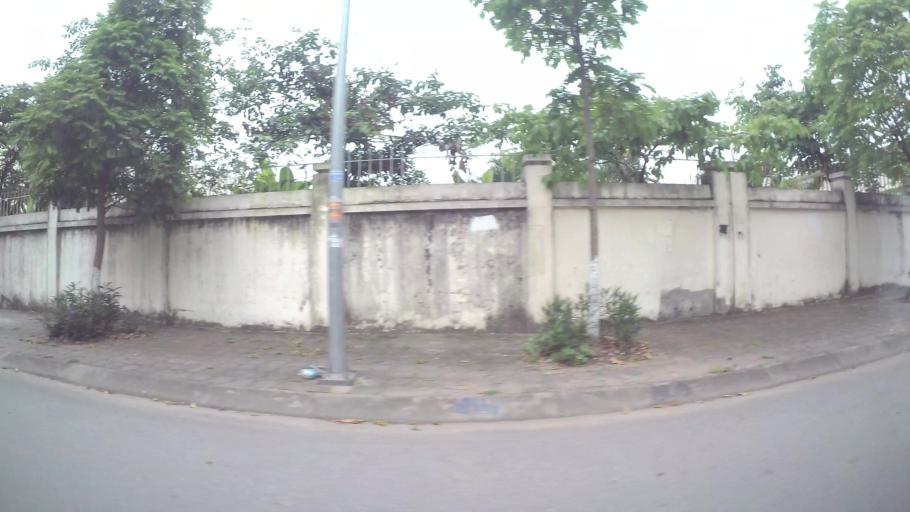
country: VN
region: Ha Noi
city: Trau Quy
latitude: 21.0445
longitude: 105.9258
